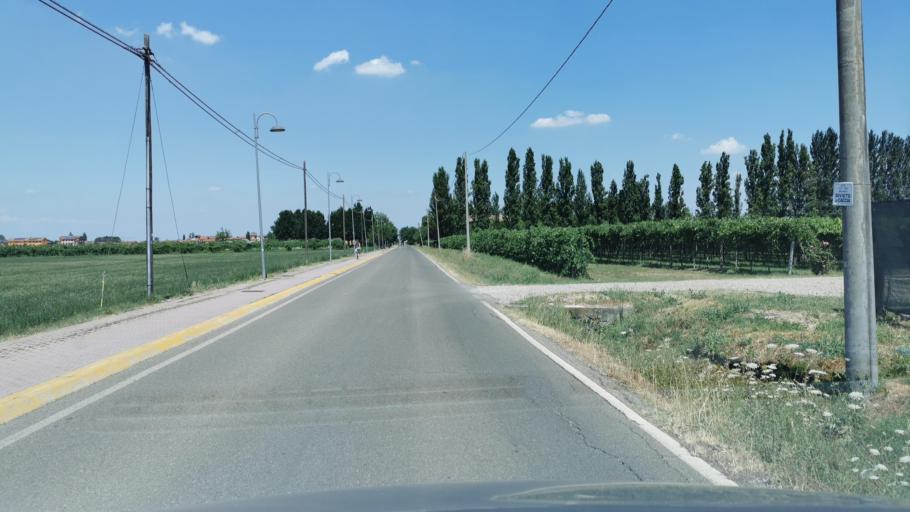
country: IT
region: Emilia-Romagna
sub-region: Provincia di Modena
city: Fossoli
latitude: 44.8101
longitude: 10.8900
